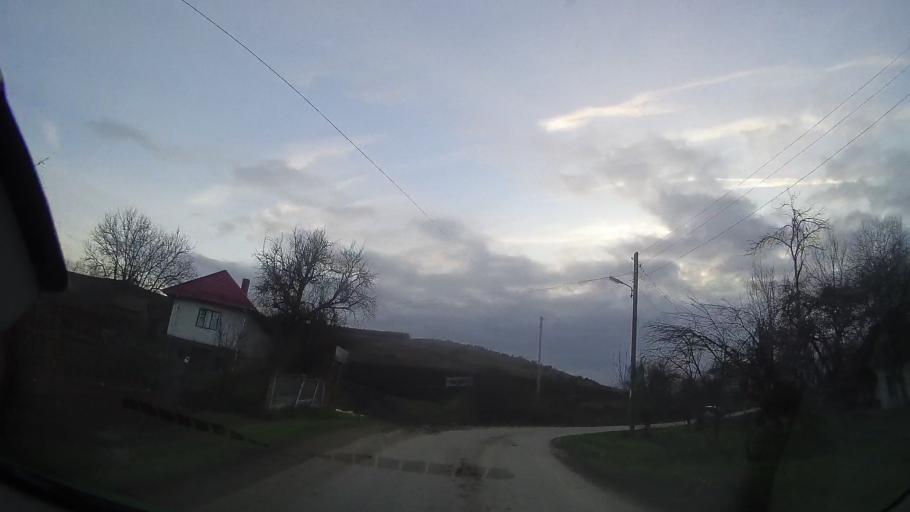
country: RO
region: Cluj
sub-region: Comuna Palatca
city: Palatca
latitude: 46.8684
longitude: 24.0127
